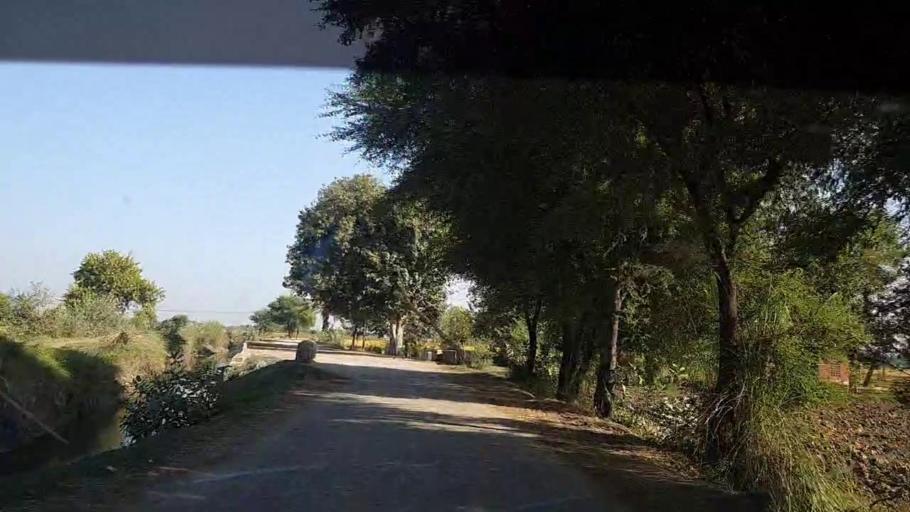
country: PK
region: Sindh
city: Larkana
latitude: 27.6219
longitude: 68.2445
